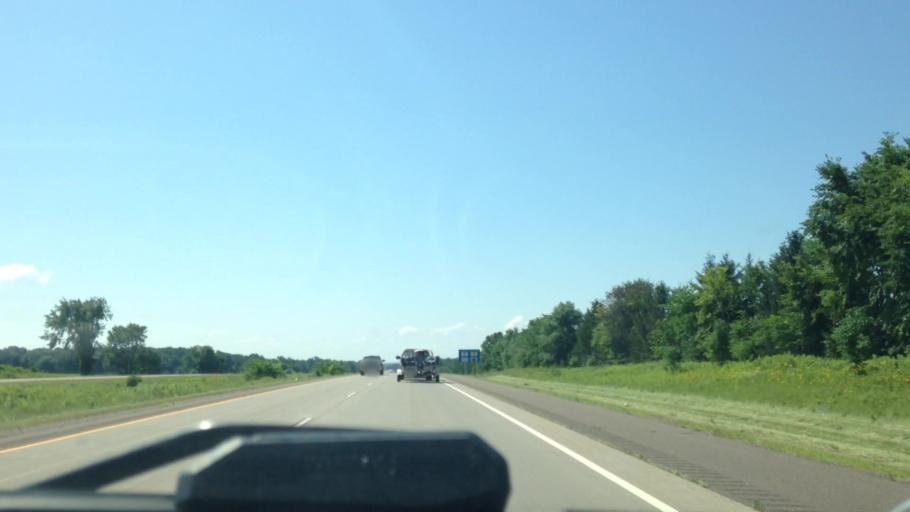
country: US
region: Wisconsin
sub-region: Barron County
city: Rice Lake
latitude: 45.4866
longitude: -91.7622
